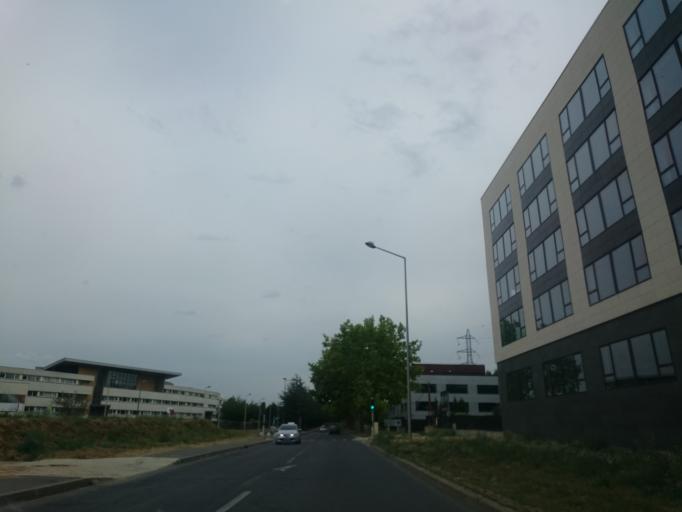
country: FR
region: Ile-de-France
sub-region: Departement de l'Essonne
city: Lisses
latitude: 48.6209
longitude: 2.4264
